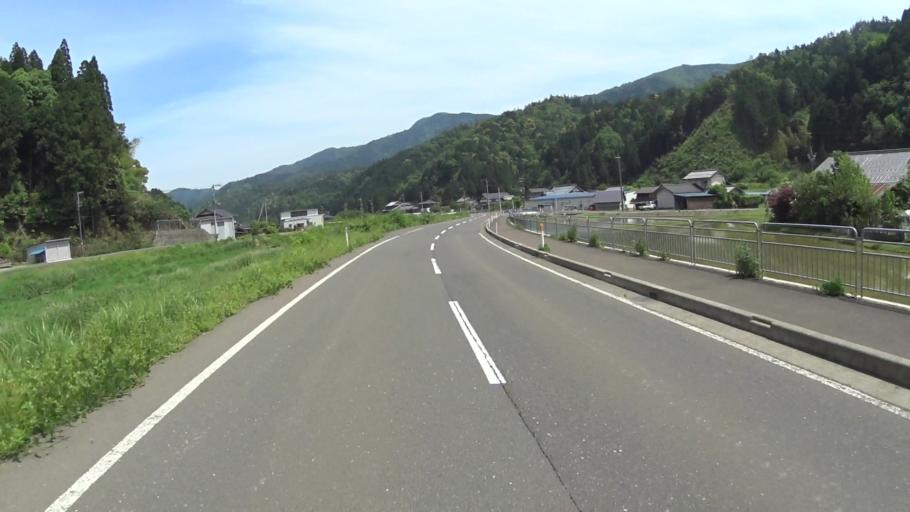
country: JP
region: Kyoto
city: Maizuru
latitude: 35.4409
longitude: 135.5239
